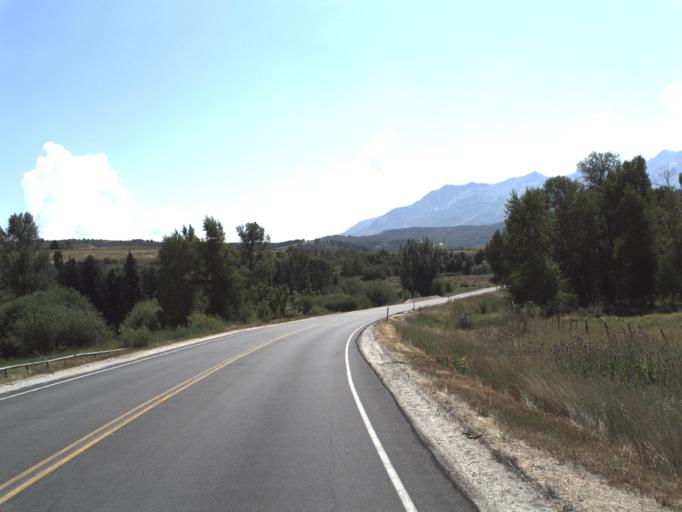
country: US
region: Utah
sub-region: Weber County
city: Wolf Creek
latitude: 41.2498
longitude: -111.7613
